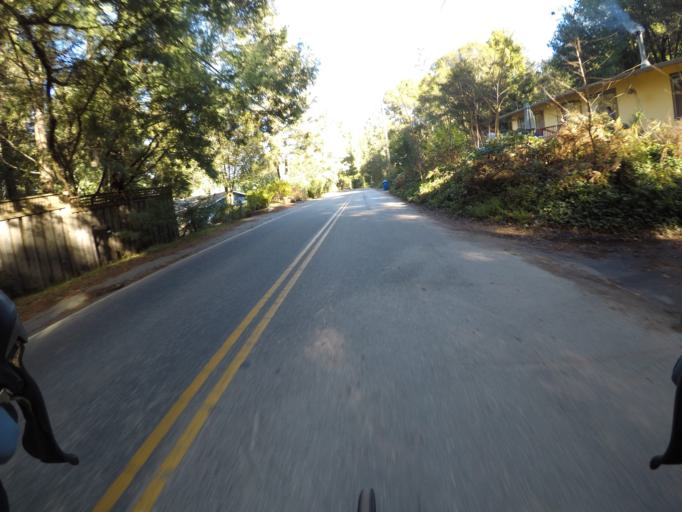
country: US
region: California
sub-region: Santa Cruz County
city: Felton
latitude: 37.0377
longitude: -122.0813
